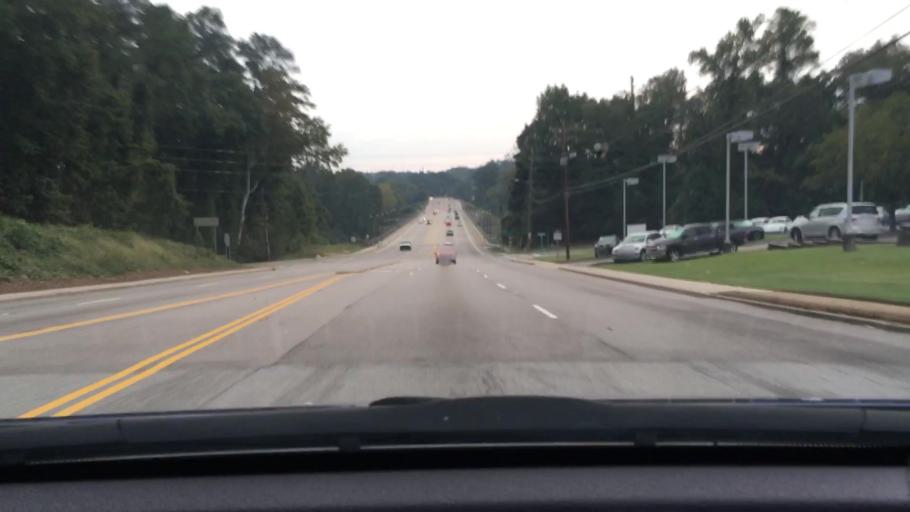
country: US
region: South Carolina
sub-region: Lexington County
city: West Columbia
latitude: 34.0253
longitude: -81.0728
